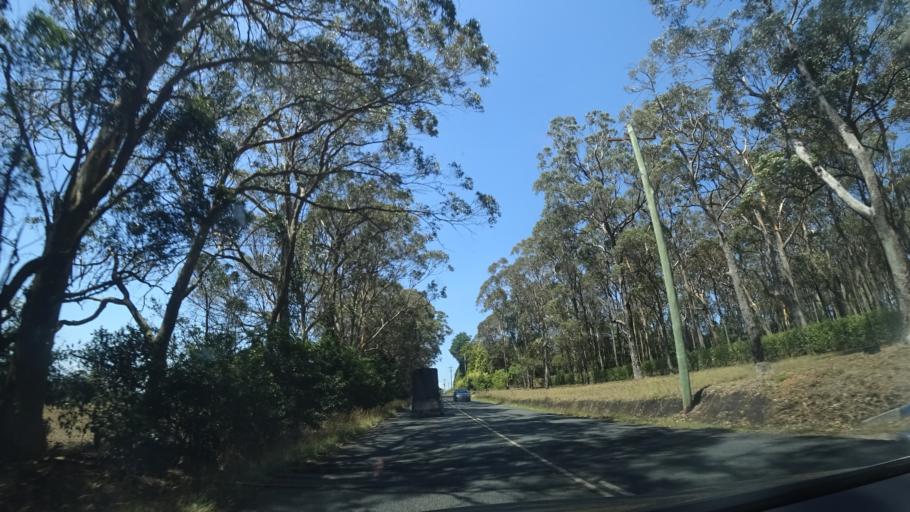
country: AU
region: New South Wales
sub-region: Wingecarribee
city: Colo Vale
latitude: -34.4028
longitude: 150.4981
